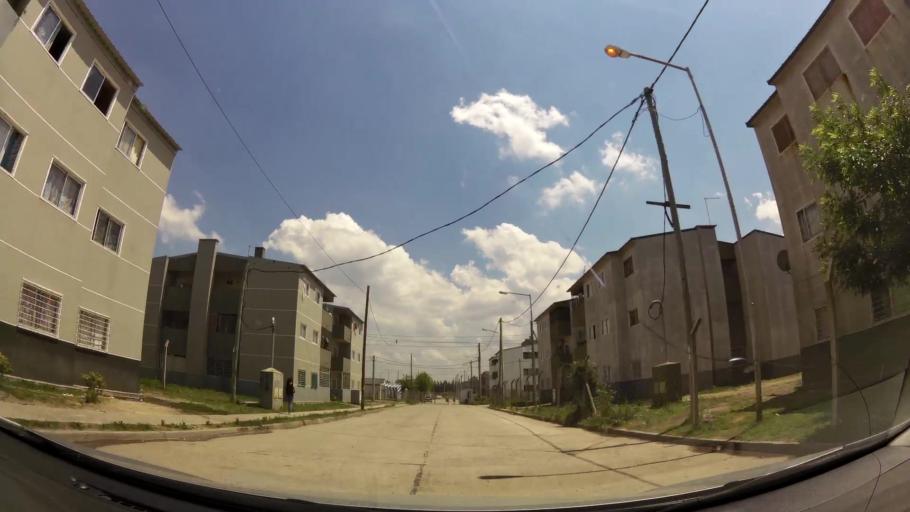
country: AR
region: Buenos Aires
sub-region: Partido de Tigre
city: Tigre
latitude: -34.4571
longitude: -58.6003
